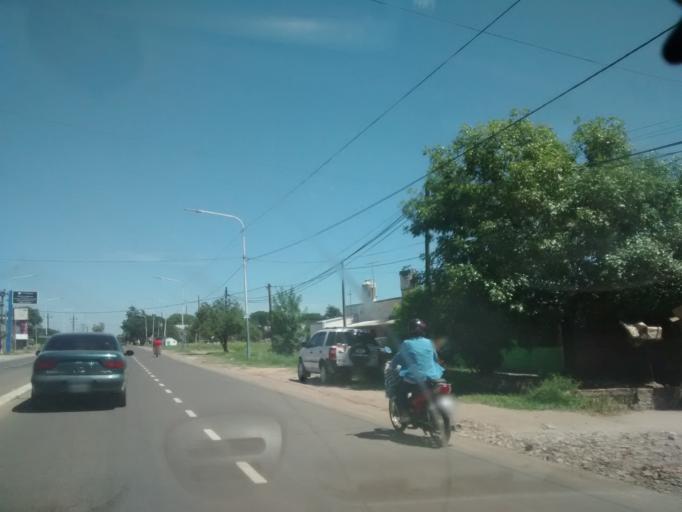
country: AR
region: Chaco
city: Fontana
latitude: -27.4242
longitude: -59.0313
